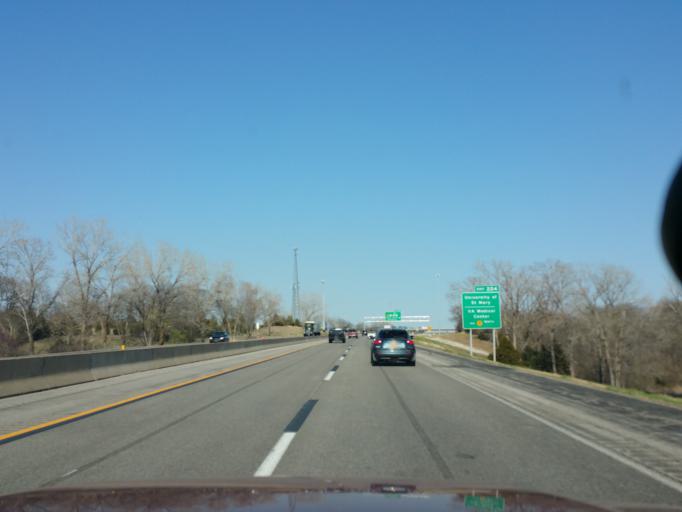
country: US
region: Kansas
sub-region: Wyandotte County
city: Bonner Springs
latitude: 39.0933
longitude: -94.8990
